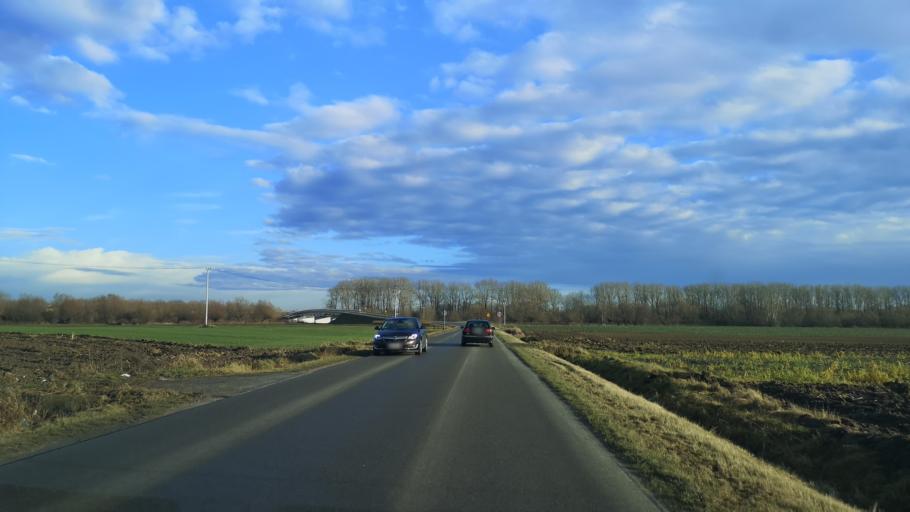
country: PL
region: Subcarpathian Voivodeship
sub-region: Powiat lezajski
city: Piskorowice
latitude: 50.2465
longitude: 22.4953
